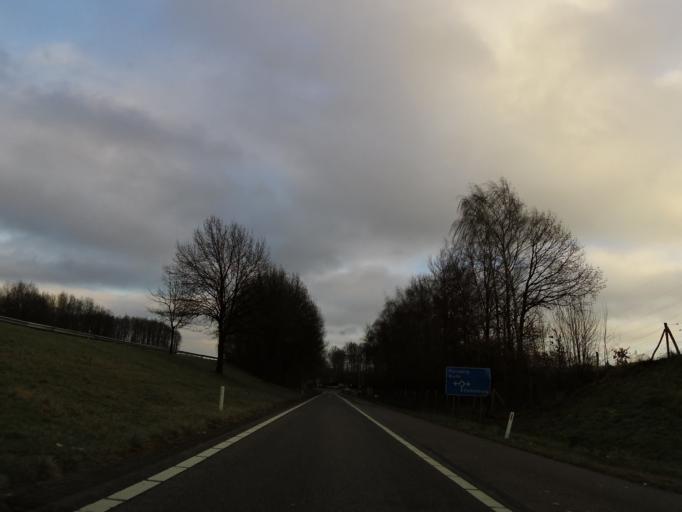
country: NL
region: Limburg
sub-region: Valkenburg aan de Geul
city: Valkenburg
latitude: 50.8821
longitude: 5.8472
